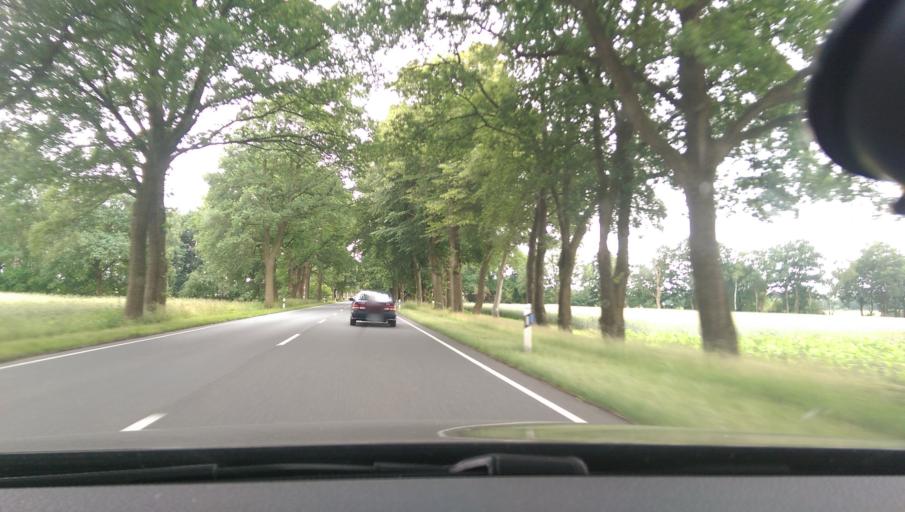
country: DE
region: Lower Saxony
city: Kirchlinteln
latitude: 52.9860
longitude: 9.2632
